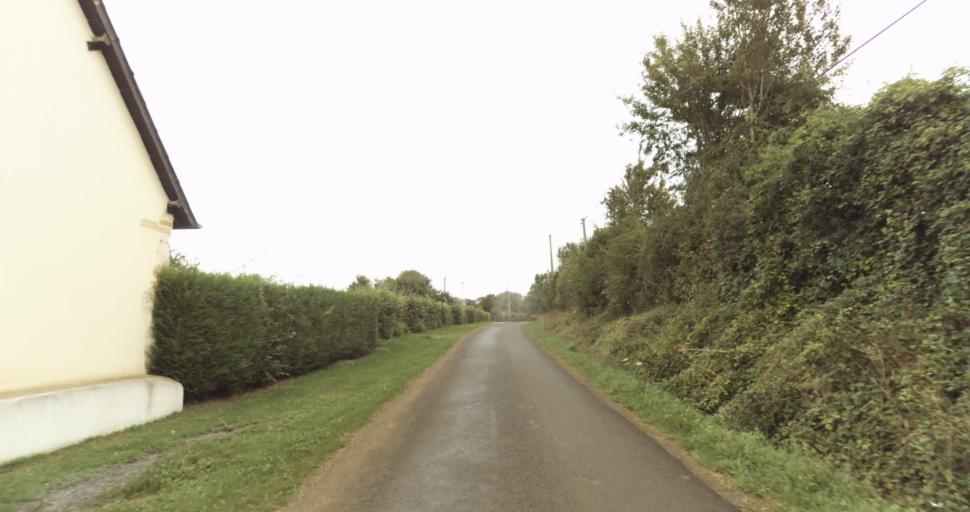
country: FR
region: Lower Normandy
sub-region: Departement de l'Orne
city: Sainte-Gauburge-Sainte-Colombe
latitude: 48.7317
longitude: 0.3785
